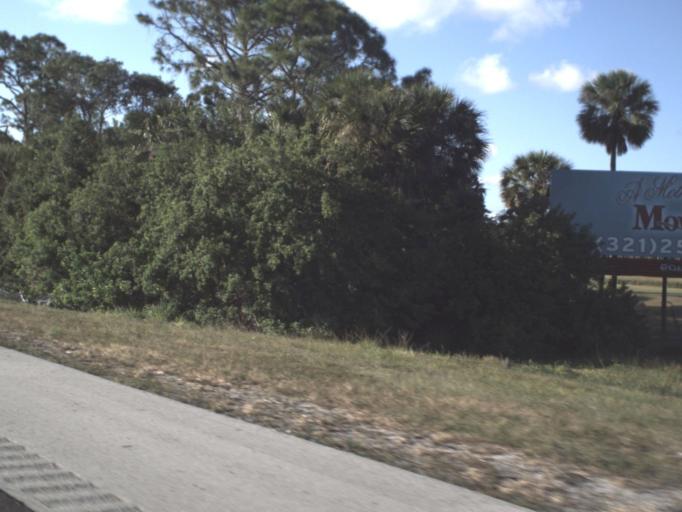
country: US
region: Florida
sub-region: Brevard County
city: Rockledge
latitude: 28.2880
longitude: -80.7368
